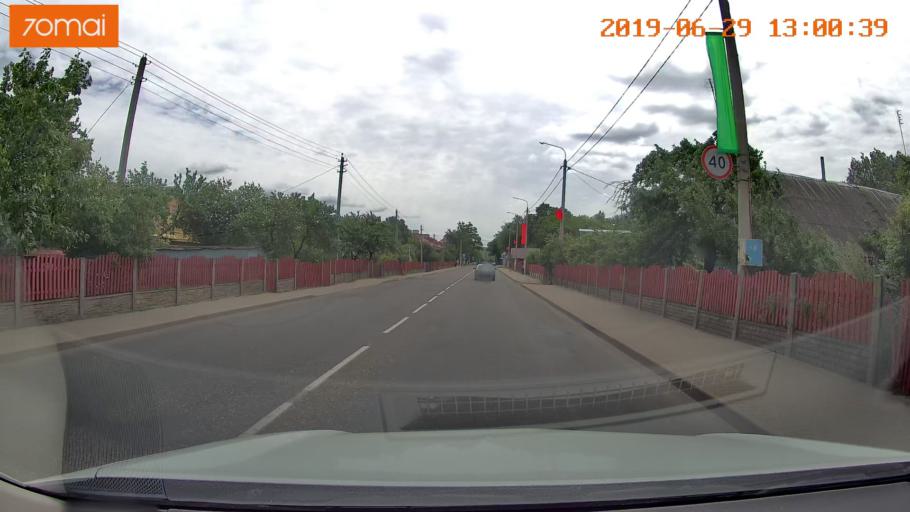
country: BY
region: Minsk
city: Slutsk
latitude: 53.0434
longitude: 27.5577
